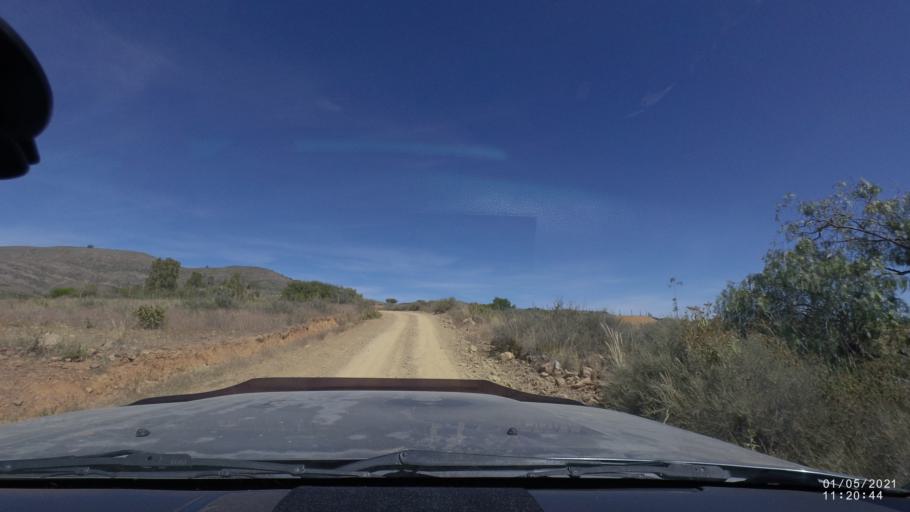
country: BO
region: Cochabamba
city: Tarata
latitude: -17.6430
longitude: -66.1242
